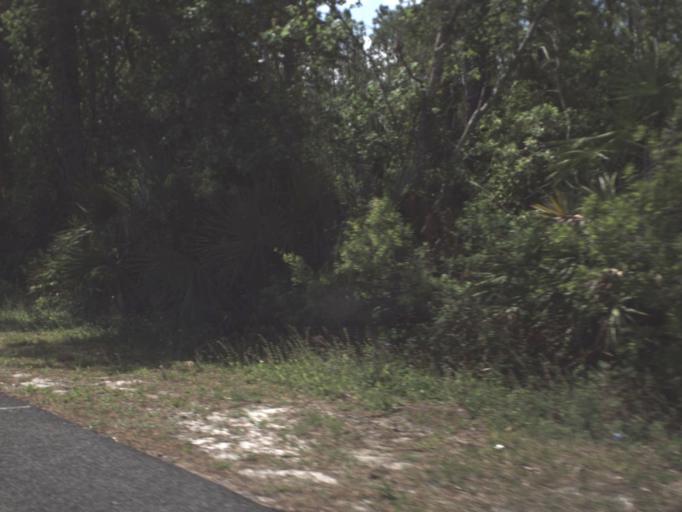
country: US
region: Florida
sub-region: Flagler County
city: Bunnell
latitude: 29.4202
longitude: -81.2119
